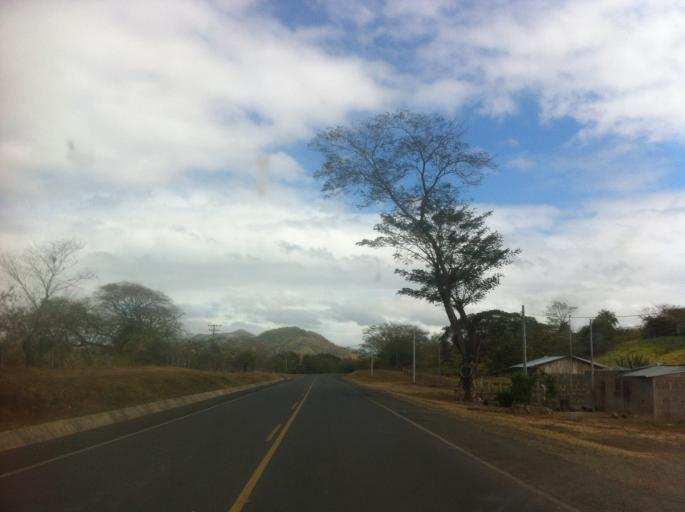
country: NI
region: Chontales
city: Acoyapa
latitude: 11.9850
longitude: -85.1700
